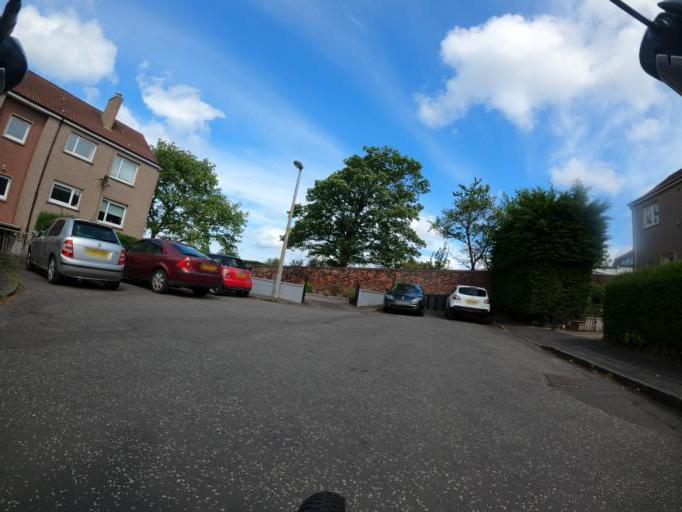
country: GB
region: Scotland
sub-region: East Lothian
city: Musselburgh
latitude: 55.9477
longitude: -3.0945
